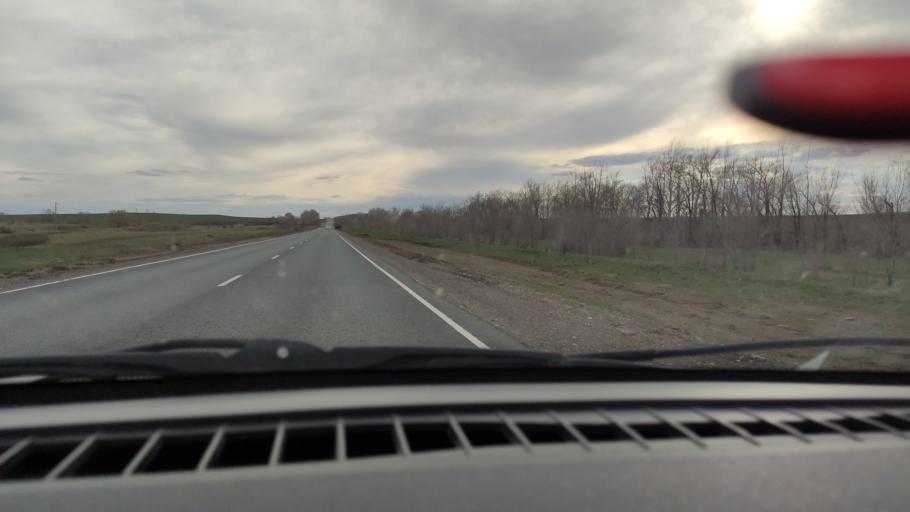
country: RU
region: Orenburg
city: Sakmara
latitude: 52.3110
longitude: 55.4558
